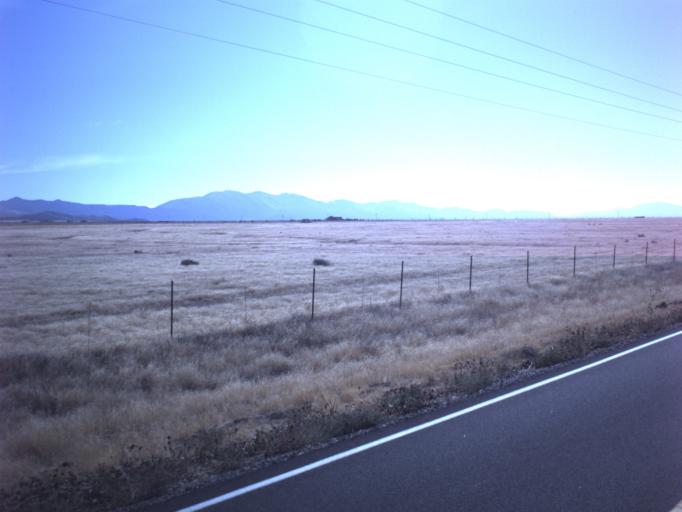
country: US
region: Utah
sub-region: Tooele County
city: Grantsville
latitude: 40.4082
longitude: -112.7483
